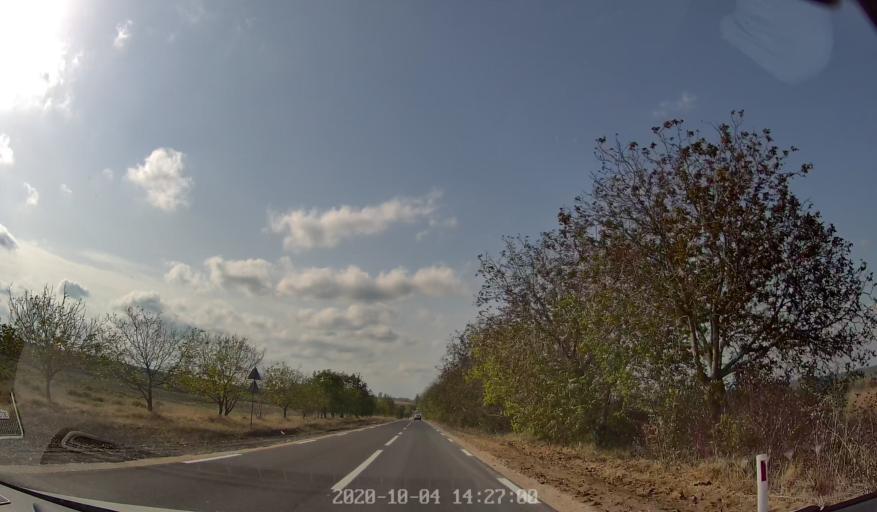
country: MD
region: Rezina
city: Saharna
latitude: 47.6306
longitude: 28.8747
